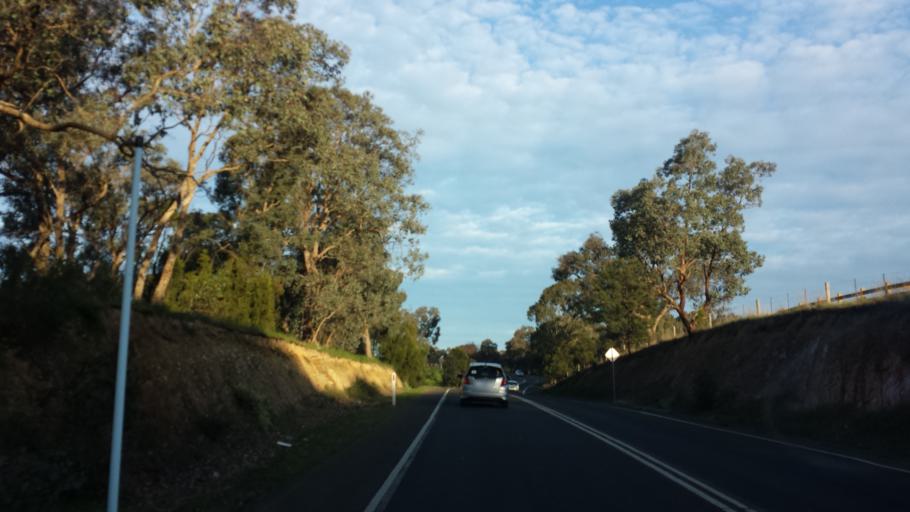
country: AU
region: Victoria
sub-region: Nillumbik
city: Wattleglen
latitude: -37.6833
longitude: 145.2084
